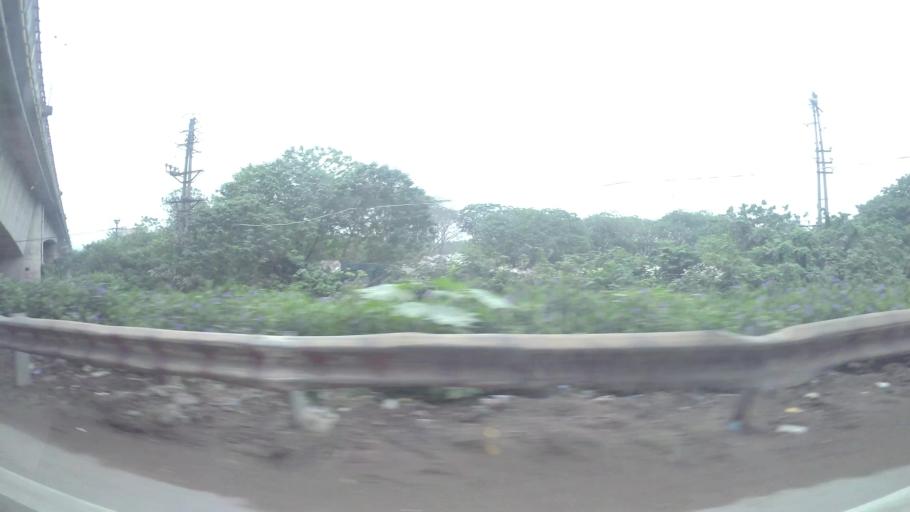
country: VN
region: Ha Noi
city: Trau Quy
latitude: 20.9862
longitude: 105.8949
